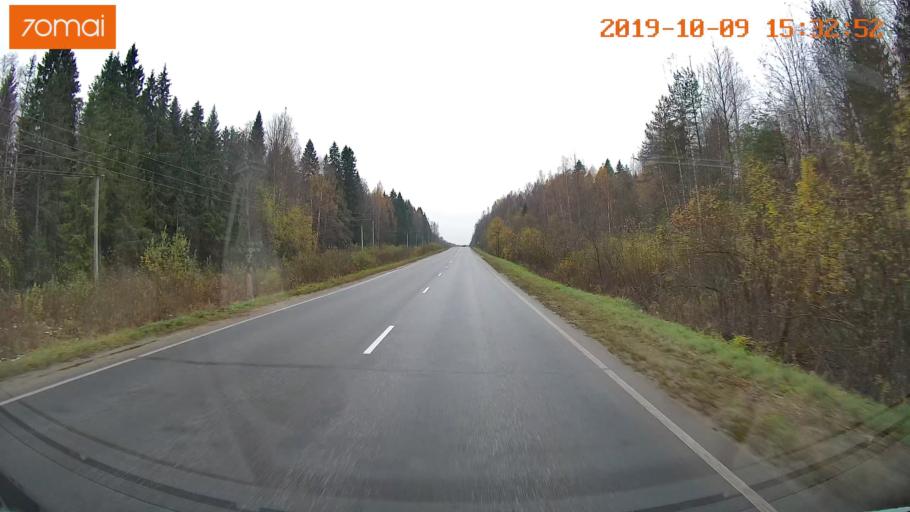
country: RU
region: Kostroma
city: Oktyabr'skiy
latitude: 57.9595
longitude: 41.2701
